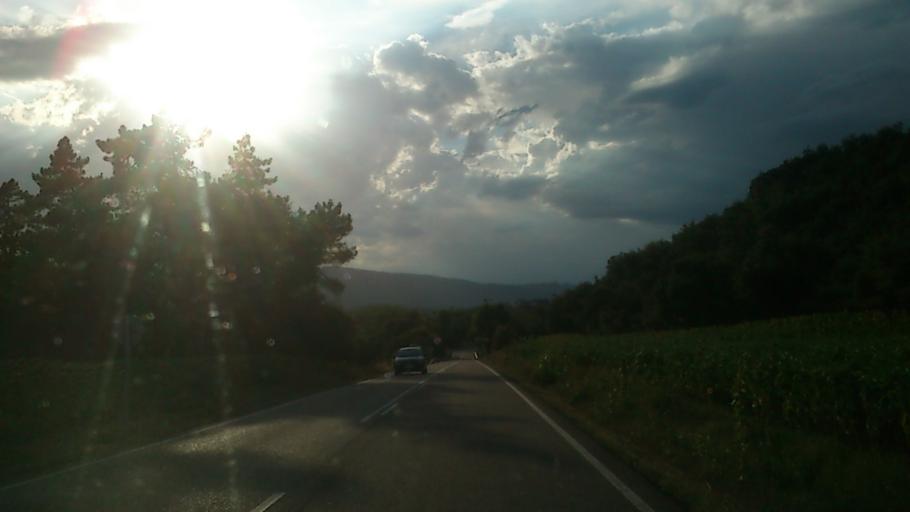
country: ES
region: Castille and Leon
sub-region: Provincia de Burgos
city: Frias
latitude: 42.7887
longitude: -3.3344
